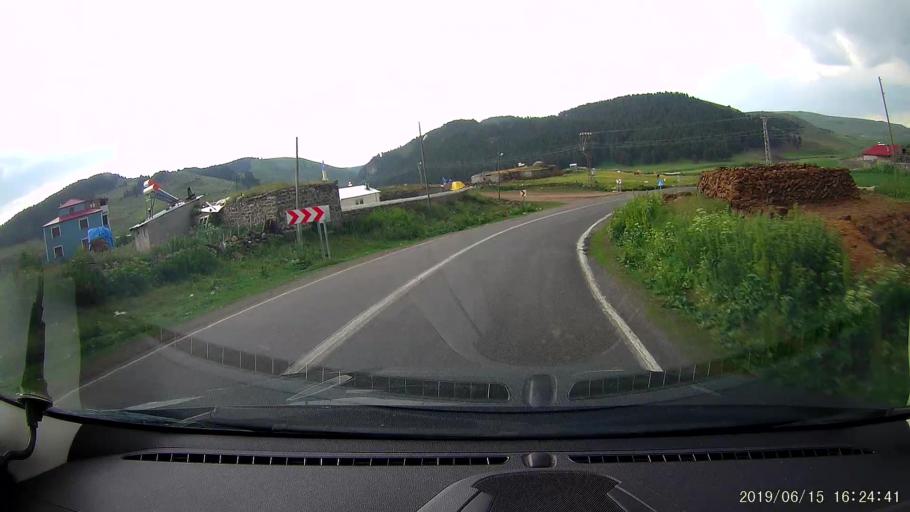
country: TR
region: Ardahan
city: Hanak
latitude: 41.1624
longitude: 42.8720
